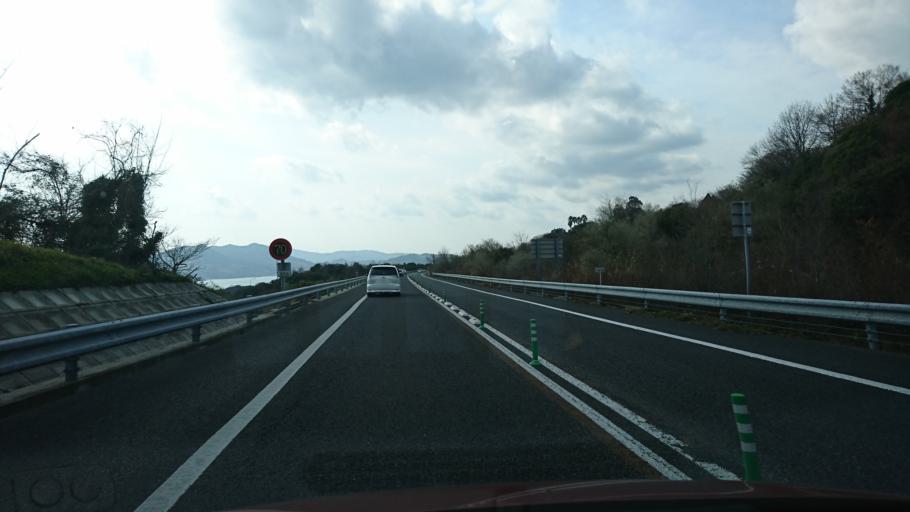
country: JP
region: Hiroshima
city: Innoshima
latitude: 34.2663
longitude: 133.0963
